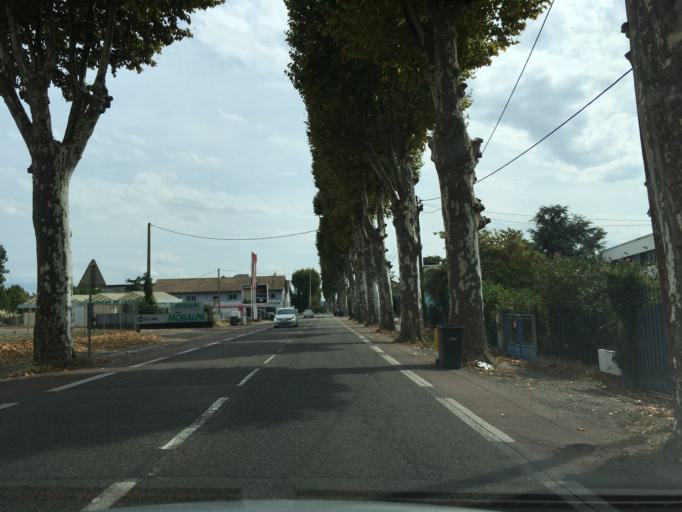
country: FR
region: Aquitaine
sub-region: Departement du Lot-et-Garonne
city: Agen
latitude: 44.1872
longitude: 0.6201
